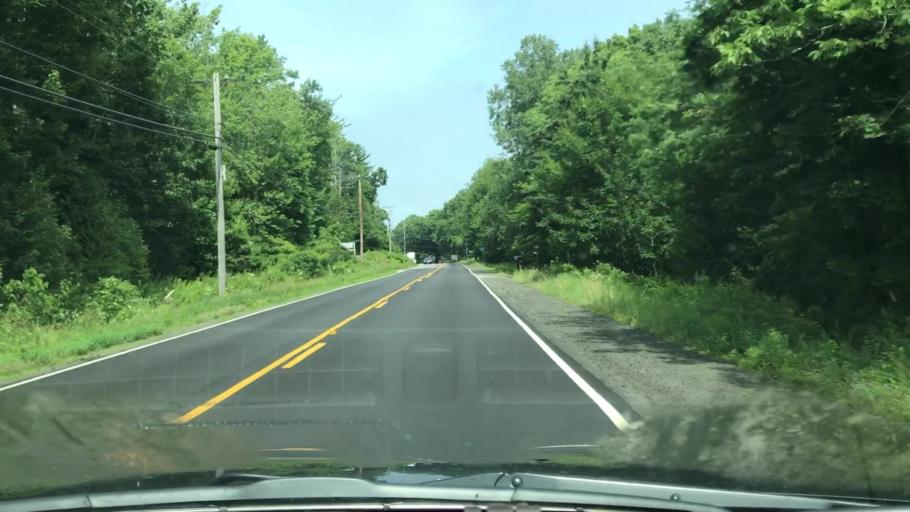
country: US
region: Maine
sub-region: Waldo County
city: Lincolnville
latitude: 44.2572
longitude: -69.0257
